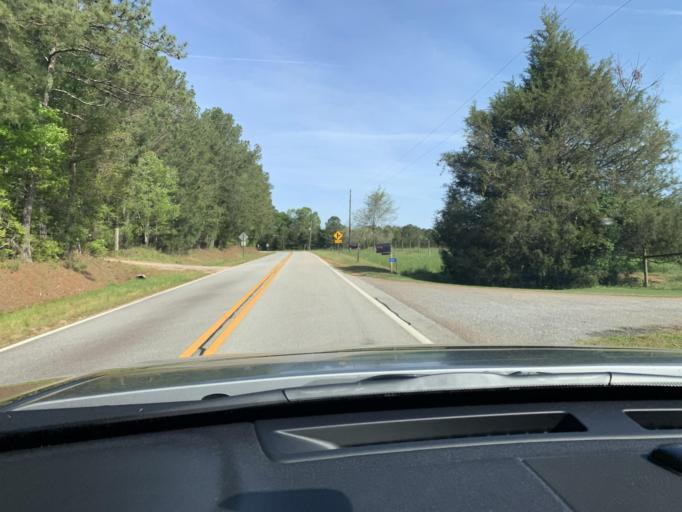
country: US
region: Georgia
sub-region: Oconee County
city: Watkinsville
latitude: 33.8145
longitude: -83.3165
